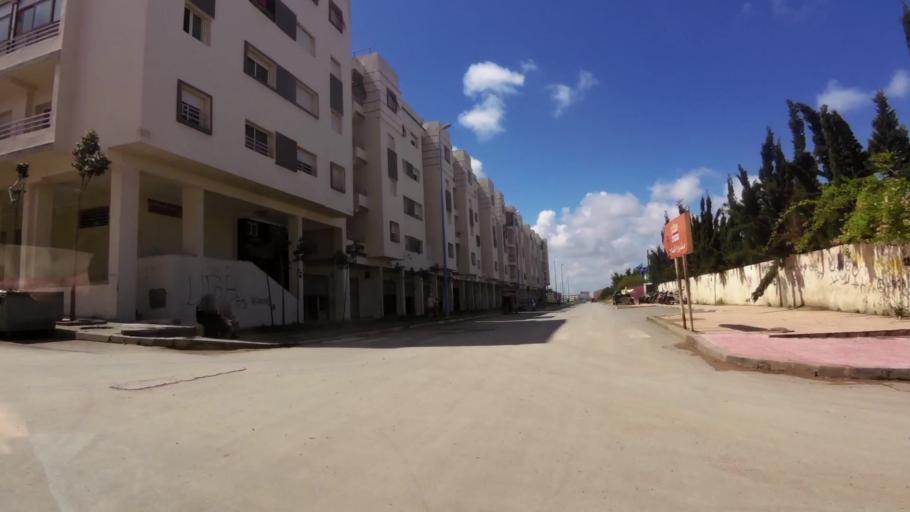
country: MA
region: Grand Casablanca
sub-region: Nouaceur
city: Dar Bouazza
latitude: 33.5340
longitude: -7.7315
